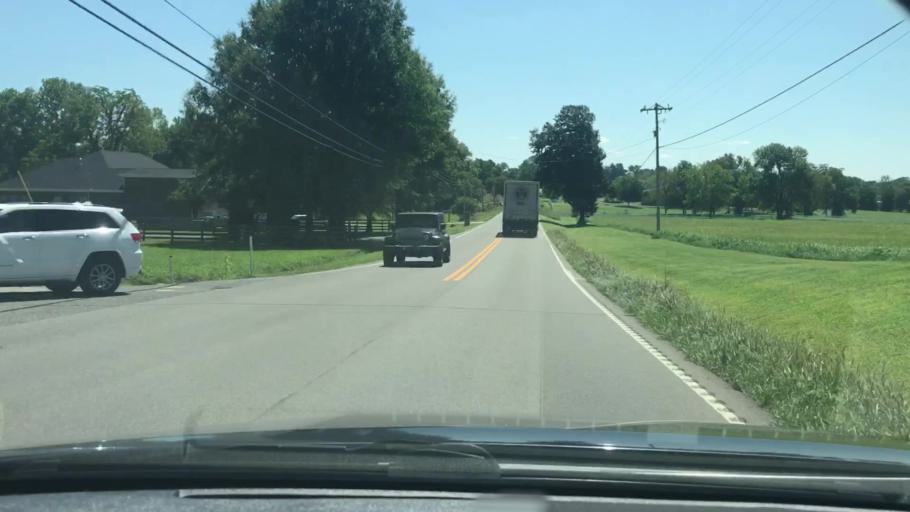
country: US
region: Tennessee
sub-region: Sumner County
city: Gallatin
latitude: 36.4168
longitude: -86.5114
